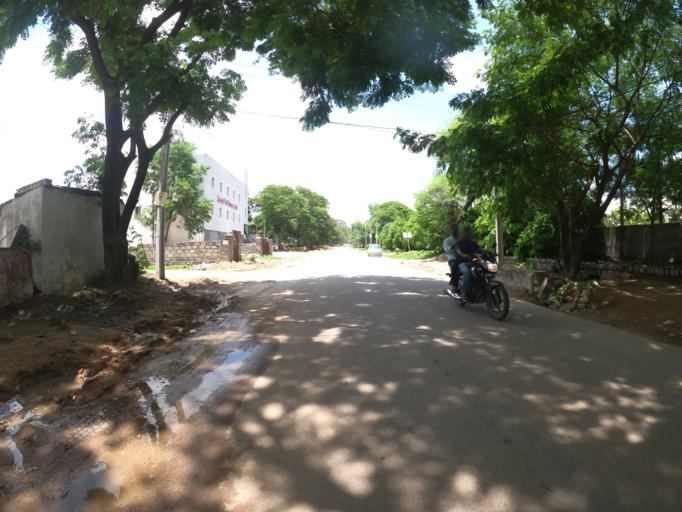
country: IN
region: Telangana
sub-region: Medak
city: Serilingampalle
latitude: 17.3846
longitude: 78.3224
